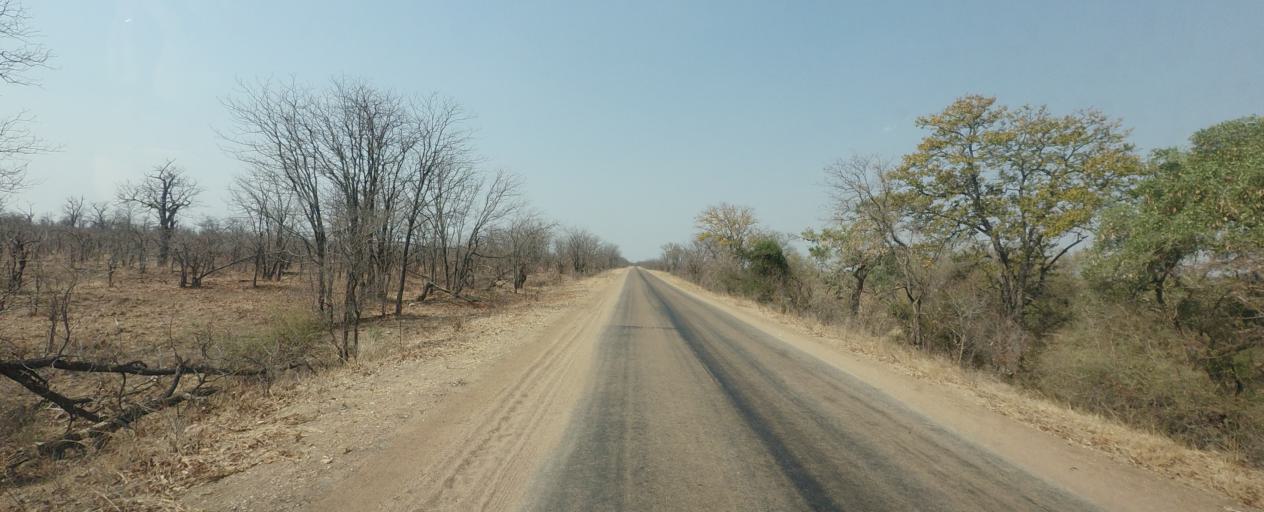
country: ZA
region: Limpopo
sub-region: Mopani District Municipality
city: Giyani
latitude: -23.1971
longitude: 31.3100
